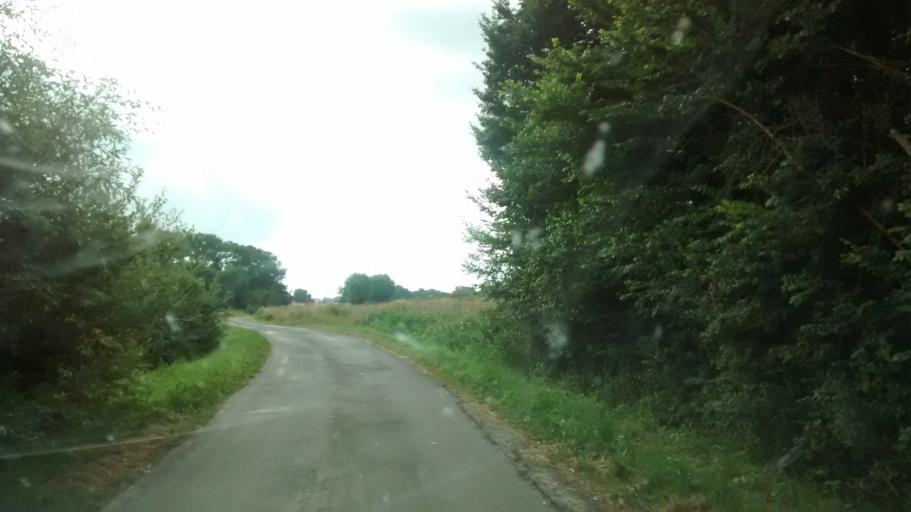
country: FR
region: Brittany
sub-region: Departement d'Ille-et-Vilaine
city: La Gouesniere
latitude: 48.6045
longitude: -1.8750
